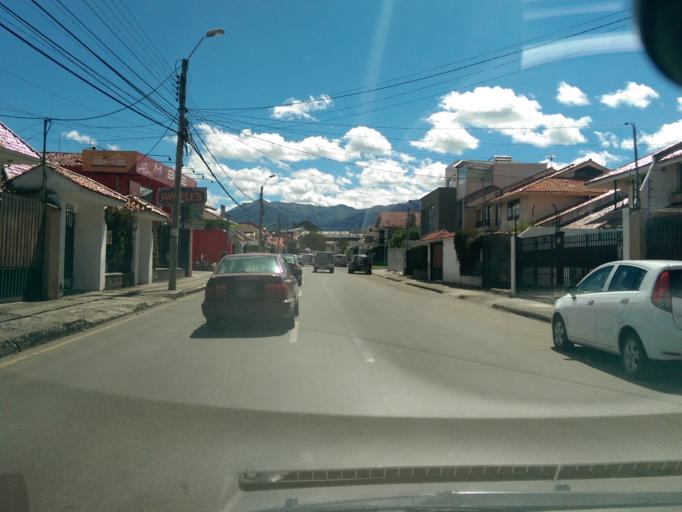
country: EC
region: Azuay
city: Cuenca
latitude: -2.9027
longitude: -79.0131
